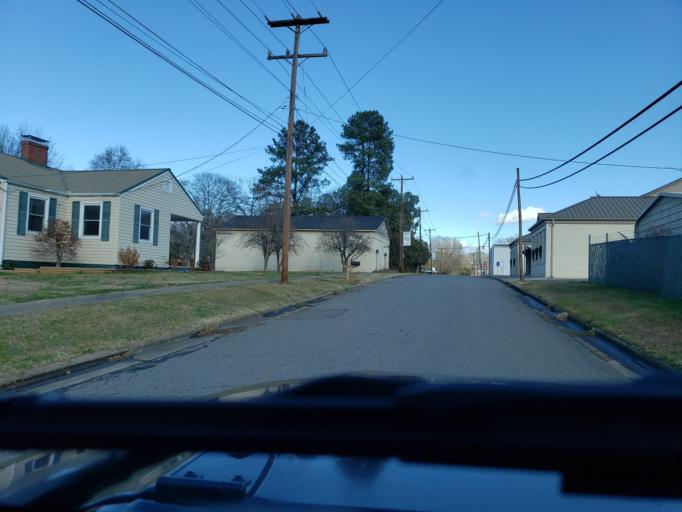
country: US
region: South Carolina
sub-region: Cherokee County
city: Blacksburg
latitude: 35.1695
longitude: -81.4505
